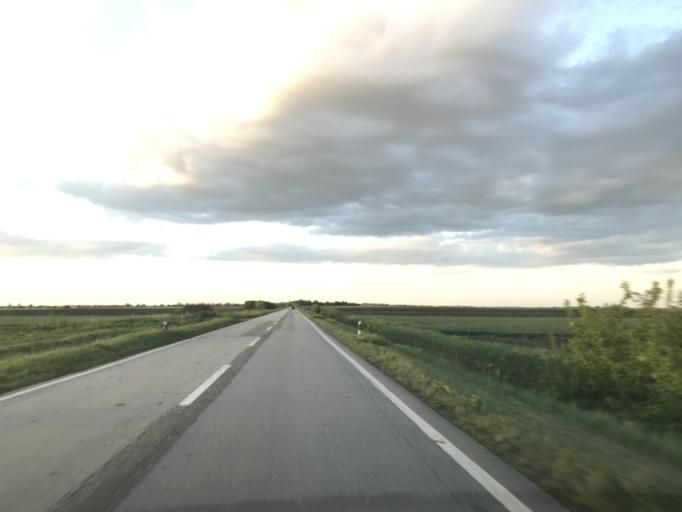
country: RS
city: Banatsko Karadordevo
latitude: 45.6007
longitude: 20.5639
